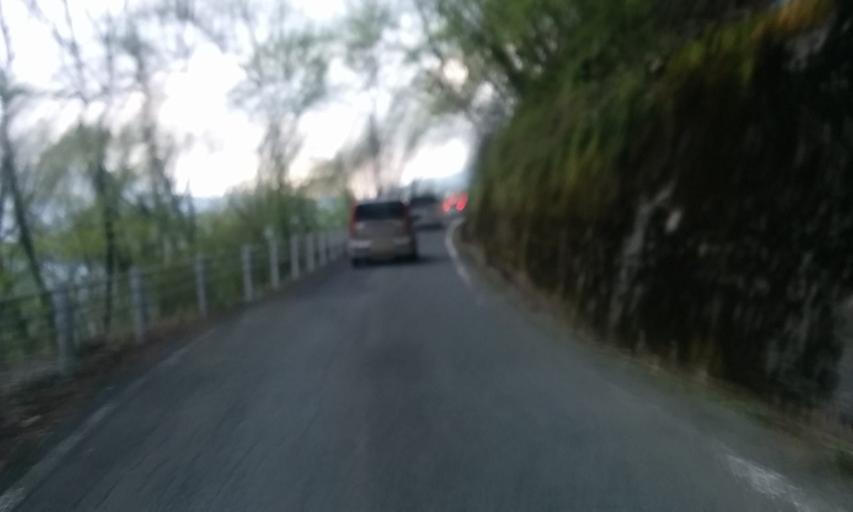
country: JP
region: Ehime
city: Saijo
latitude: 33.7926
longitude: 133.2693
